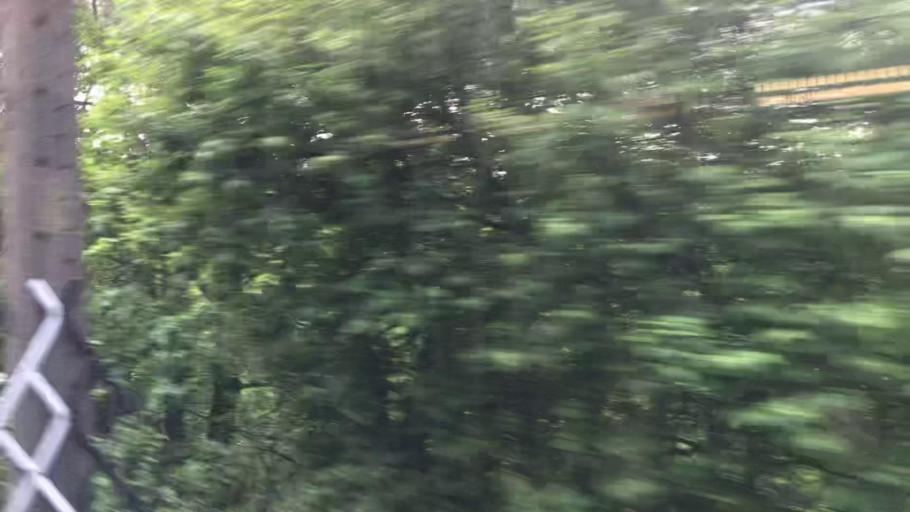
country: PL
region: Lower Silesian Voivodeship
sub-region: Powiat walbrzyski
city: Walbrzych
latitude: 50.8086
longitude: 16.3002
